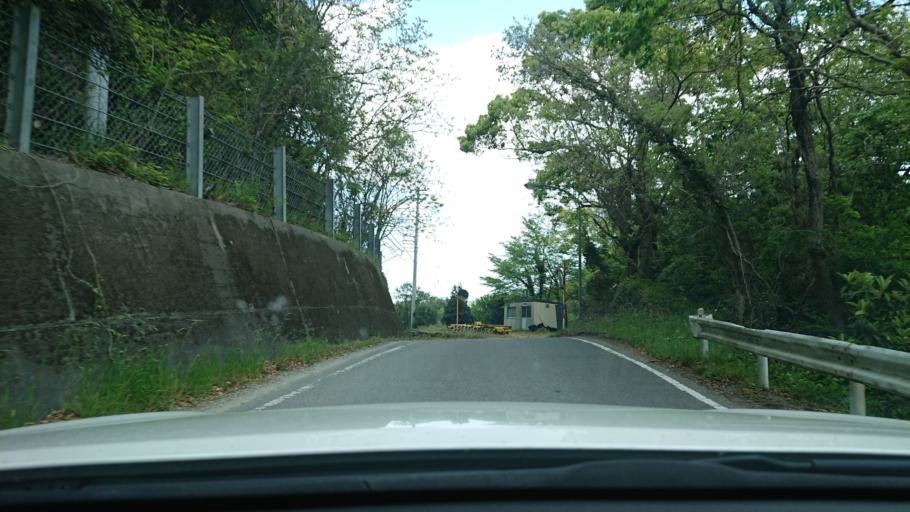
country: JP
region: Tokushima
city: Komatsushimacho
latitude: 33.9858
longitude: 134.5447
